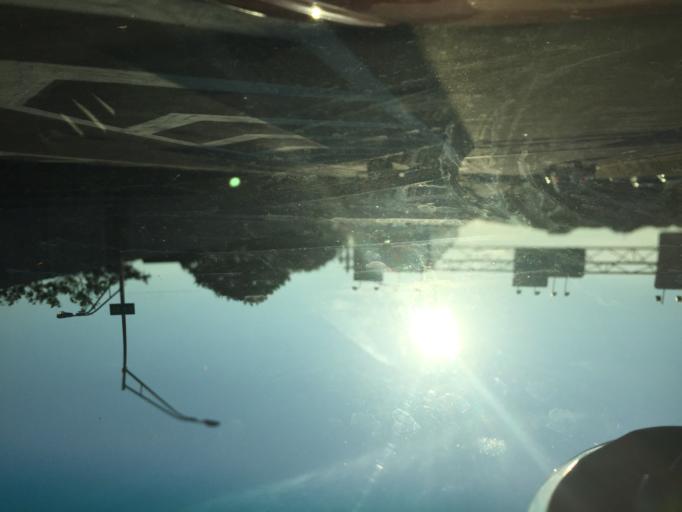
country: US
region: New York
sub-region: Queens County
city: Long Island City
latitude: 40.7387
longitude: -73.9022
